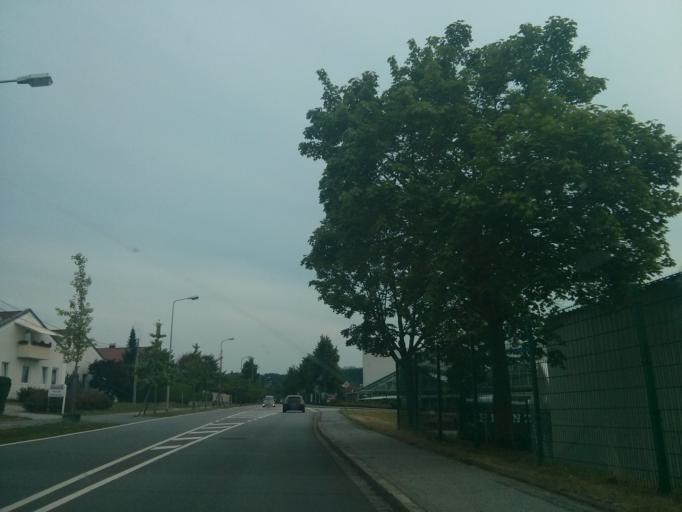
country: DE
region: Bavaria
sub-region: Lower Bavaria
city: Deggendorf
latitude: 48.8516
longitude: 12.9639
